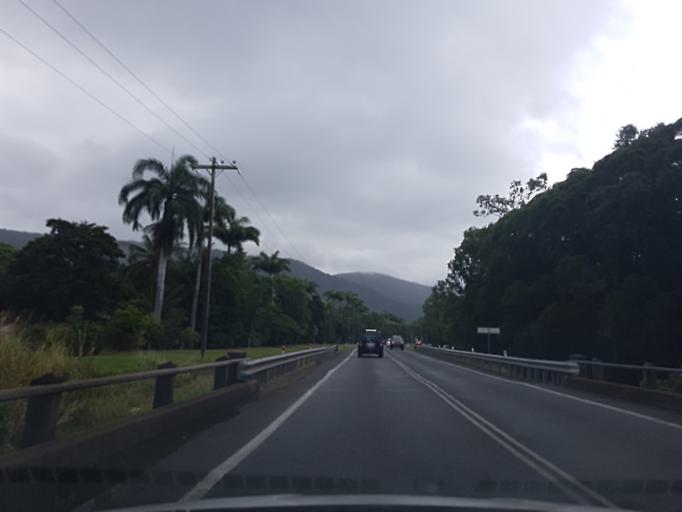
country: AU
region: Queensland
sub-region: Cairns
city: Trinity Beach
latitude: -16.7876
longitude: 145.6755
